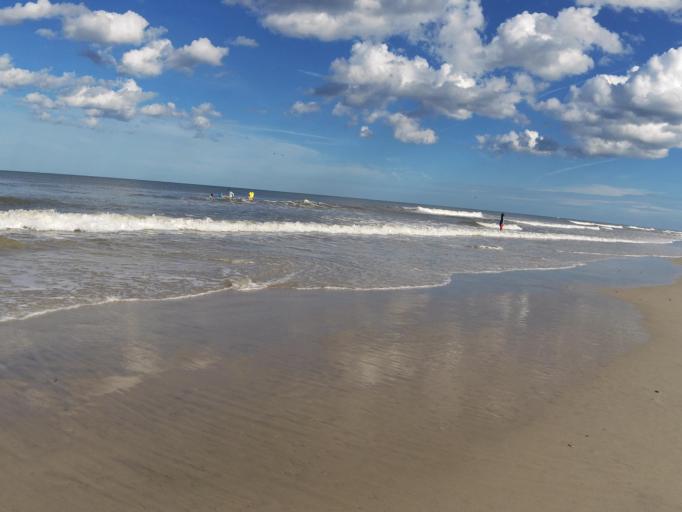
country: US
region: Florida
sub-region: Nassau County
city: Fernandina Beach
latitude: 30.6790
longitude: -81.4284
